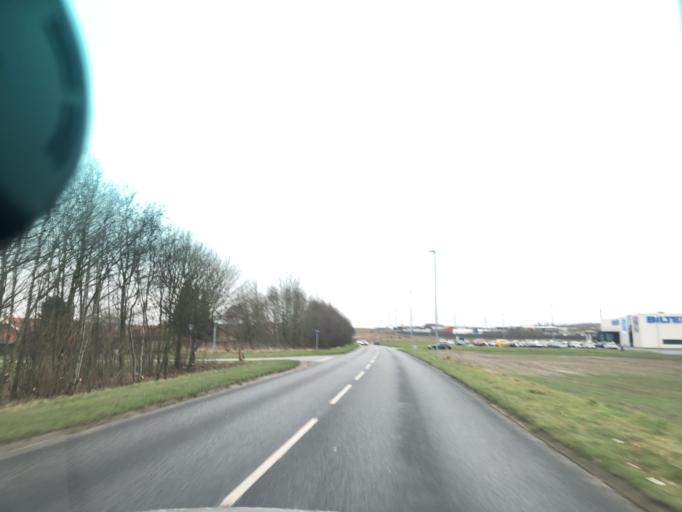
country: DK
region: Central Jutland
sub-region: Randers Kommune
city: Randers
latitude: 56.4249
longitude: 10.0643
